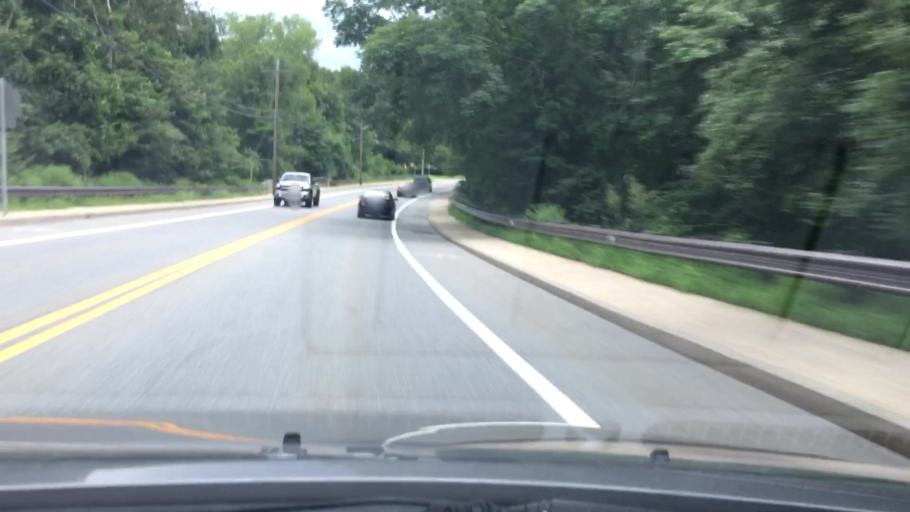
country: US
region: Rhode Island
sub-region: Providence County
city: Cumberland
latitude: 41.9795
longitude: -71.3945
